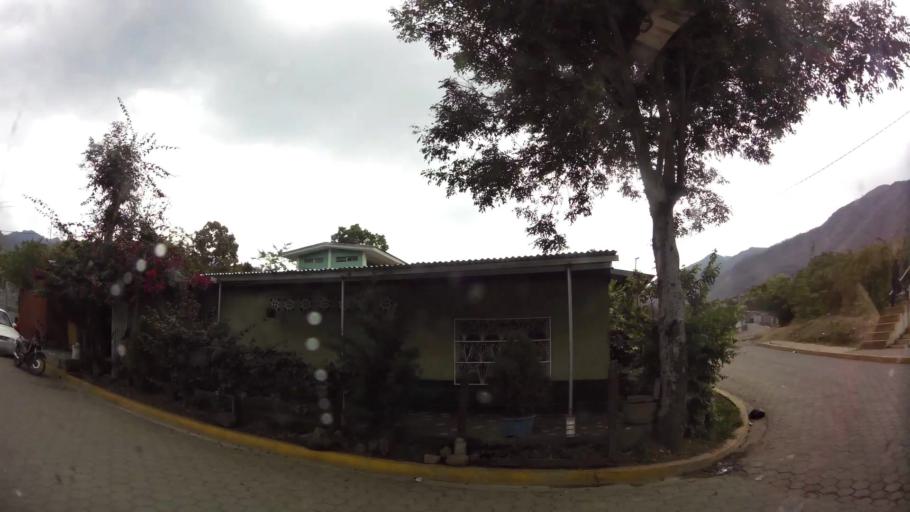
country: NI
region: Jinotega
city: Jinotega
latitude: 13.0978
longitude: -86.0042
